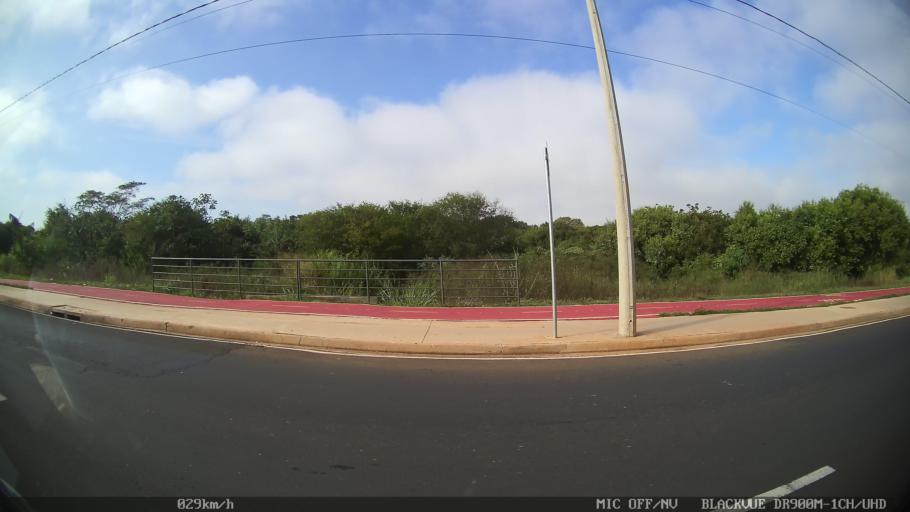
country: BR
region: Sao Paulo
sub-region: Sao Jose Do Rio Preto
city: Sao Jose do Rio Preto
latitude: -20.8074
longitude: -49.4283
